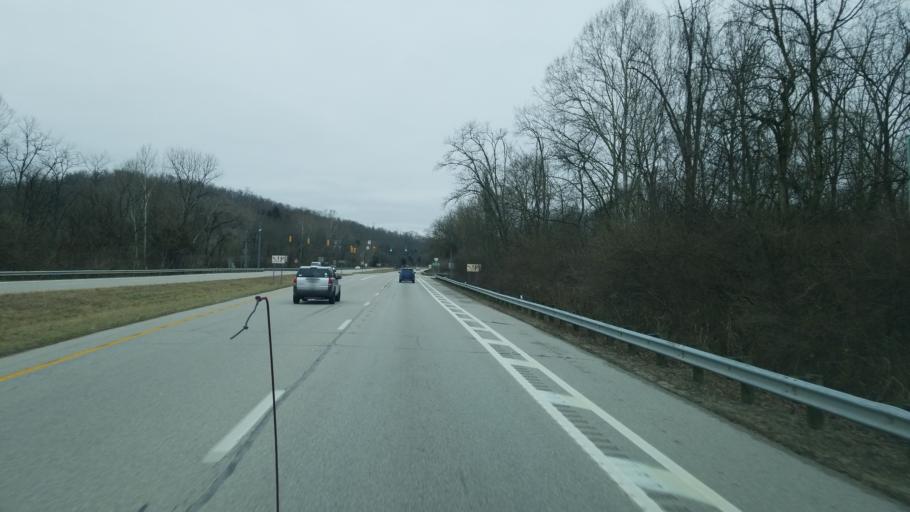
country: US
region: Ohio
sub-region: Clermont County
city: Withamsville
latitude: 39.0108
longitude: -84.3042
